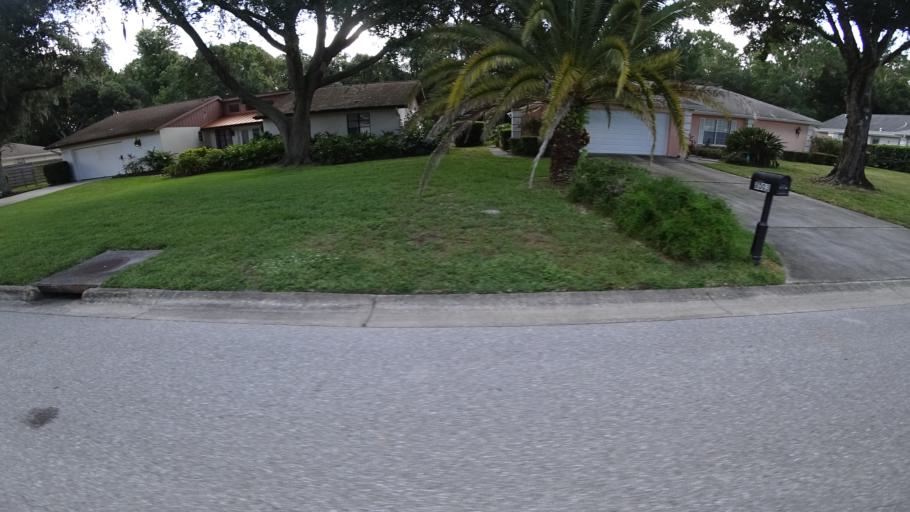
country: US
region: Florida
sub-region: Sarasota County
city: Desoto Lakes
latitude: 27.3980
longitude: -82.4937
